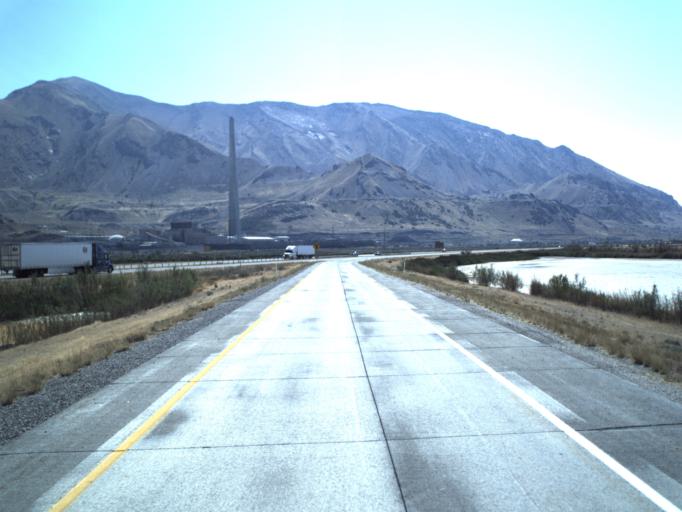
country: US
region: Utah
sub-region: Salt Lake County
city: Magna
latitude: 40.7437
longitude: -112.1862
